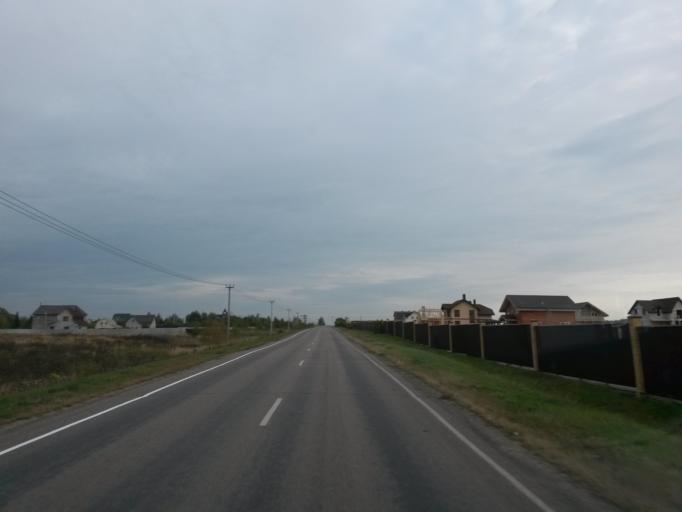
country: RU
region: Moskovskaya
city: Barybino
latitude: 55.2412
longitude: 37.7968
